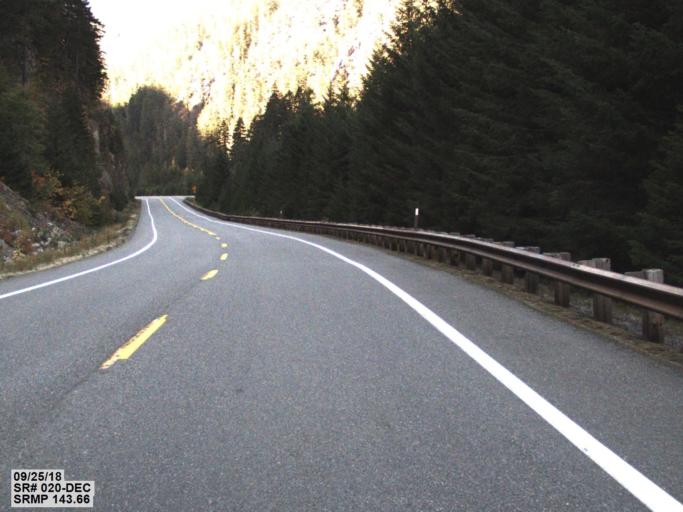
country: US
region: Washington
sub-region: Snohomish County
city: Darrington
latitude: 48.6819
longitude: -120.8832
